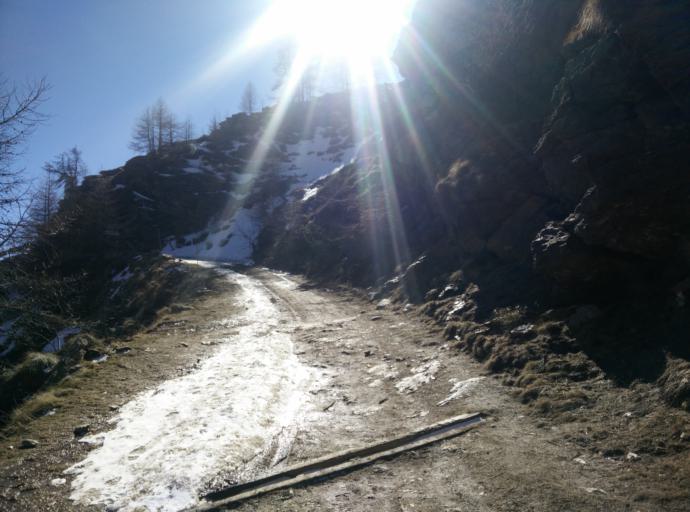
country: IT
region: Piedmont
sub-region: Provincia di Torino
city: Roure
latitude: 45.0467
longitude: 7.1193
